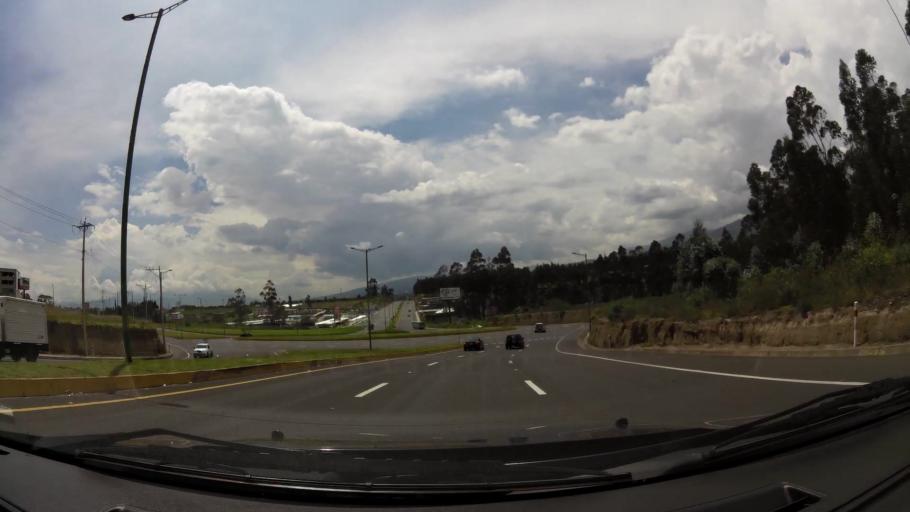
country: EC
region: Pichincha
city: Sangolqui
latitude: -0.1910
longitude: -78.3391
